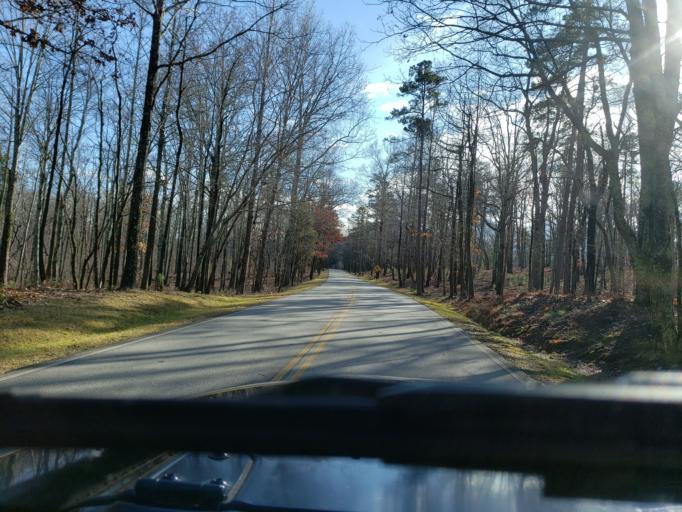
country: US
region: North Carolina
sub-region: Cleveland County
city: White Plains
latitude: 35.1456
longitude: -81.3877
